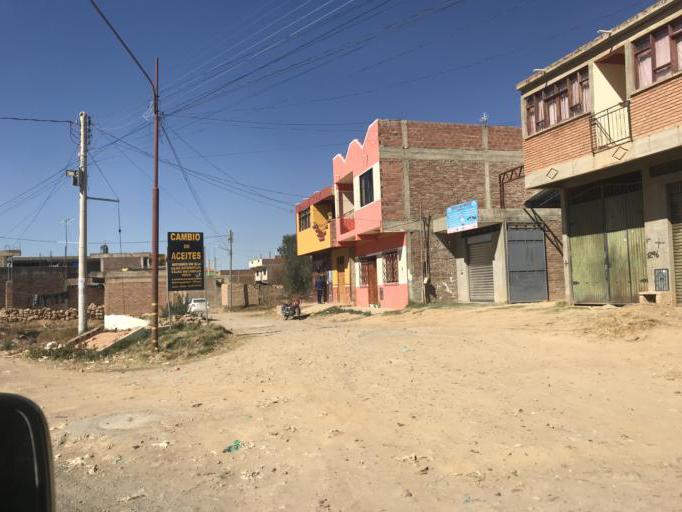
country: BO
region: Cochabamba
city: Cliza
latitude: -17.5852
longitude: -65.9182
